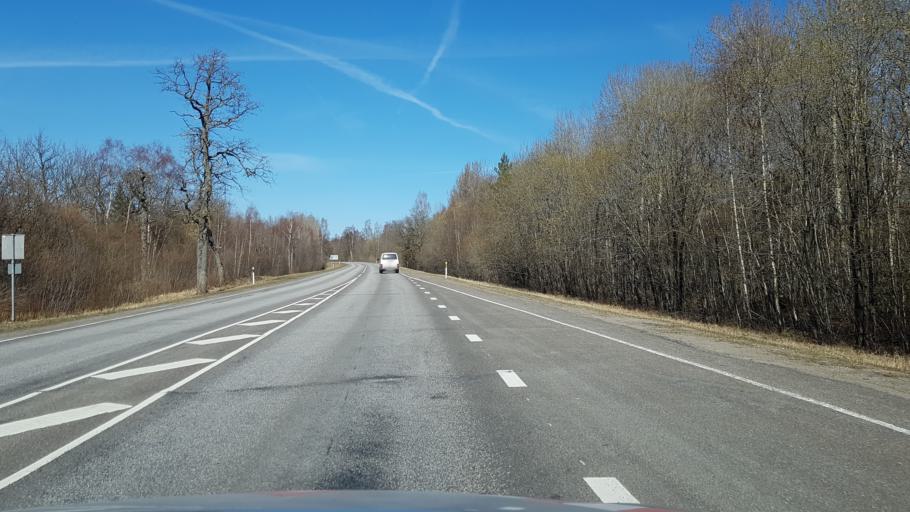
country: EE
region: Laeaene
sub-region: Lihula vald
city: Lihula
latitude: 58.6296
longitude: 23.6845
